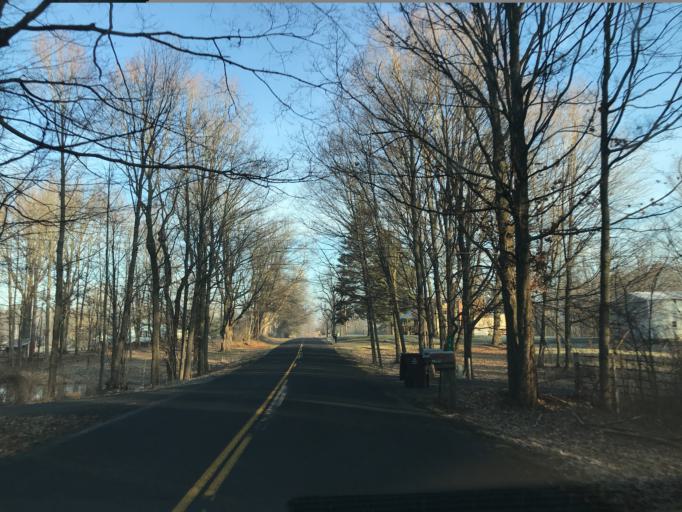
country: US
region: Michigan
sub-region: Ingham County
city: Holt
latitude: 42.5780
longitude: -84.5822
